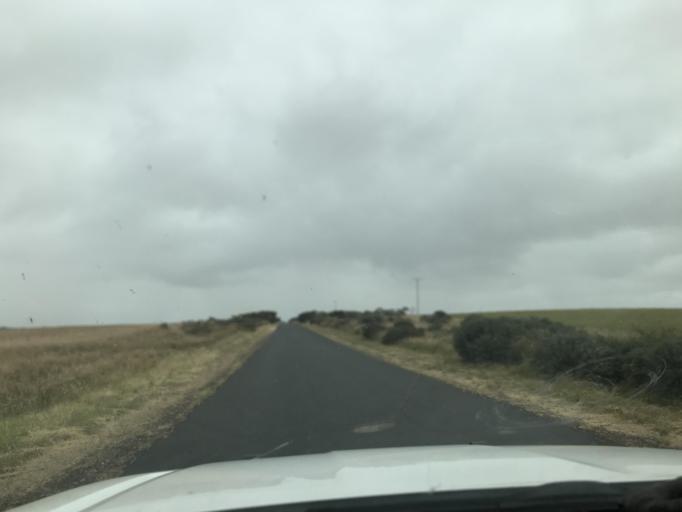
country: AU
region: South Australia
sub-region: Tatiara
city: Bordertown
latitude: -36.1175
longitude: 141.0403
